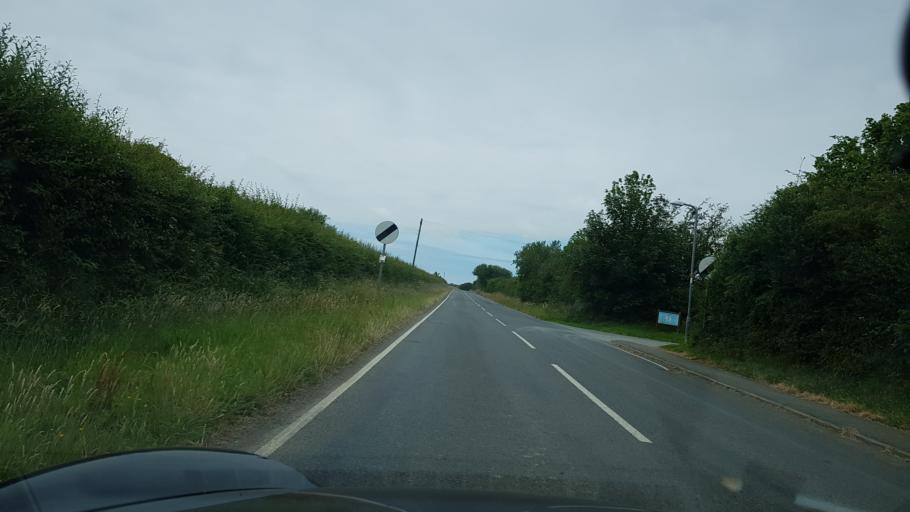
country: GB
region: Wales
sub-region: Pembrokeshire
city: Haverfordwest
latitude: 51.7968
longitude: -4.9920
